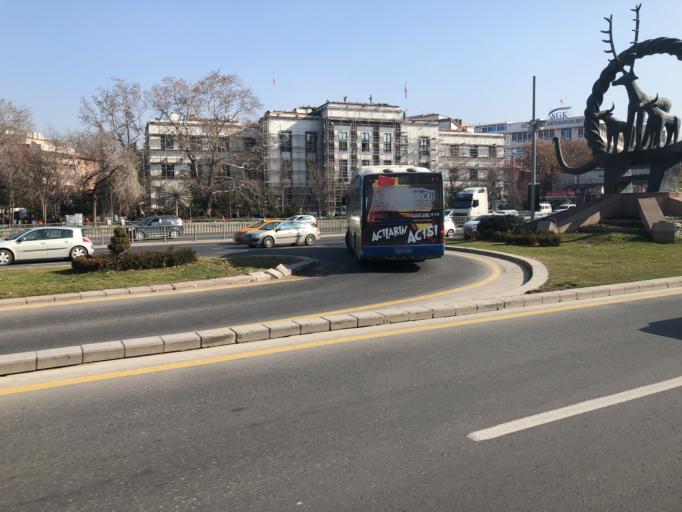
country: TR
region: Ankara
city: Ankara
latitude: 39.9273
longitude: 32.8549
